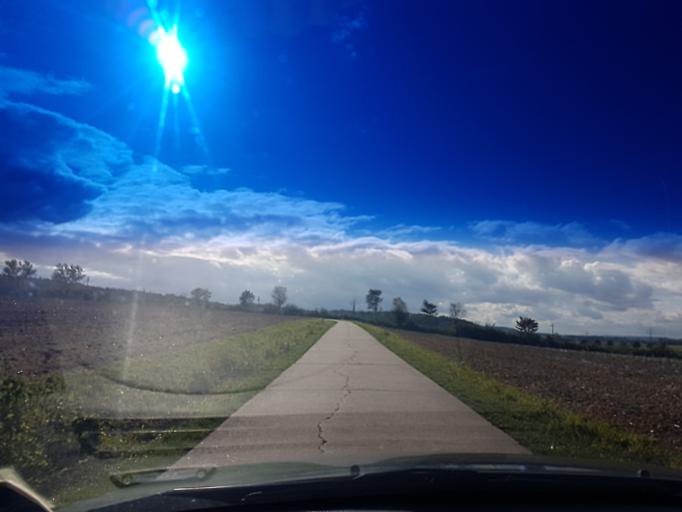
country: DE
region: Bavaria
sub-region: Regierungsbezirk Mittelfranken
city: Muhlhausen
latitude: 49.7457
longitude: 10.7862
